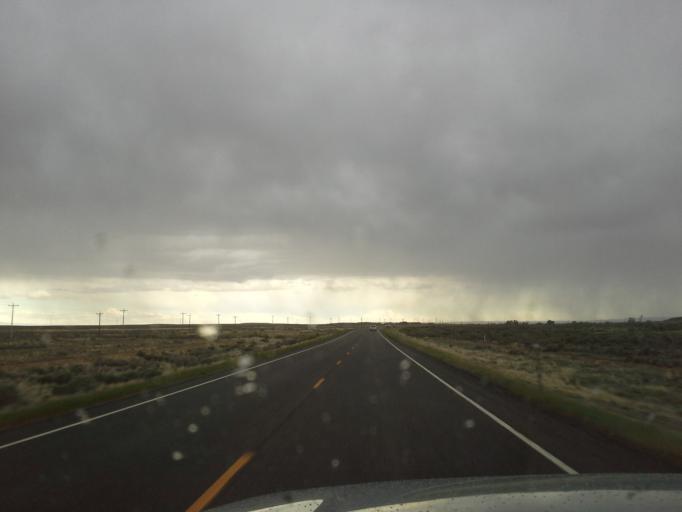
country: US
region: Wyoming
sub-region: Park County
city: Powell
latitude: 45.0259
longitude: -108.6340
